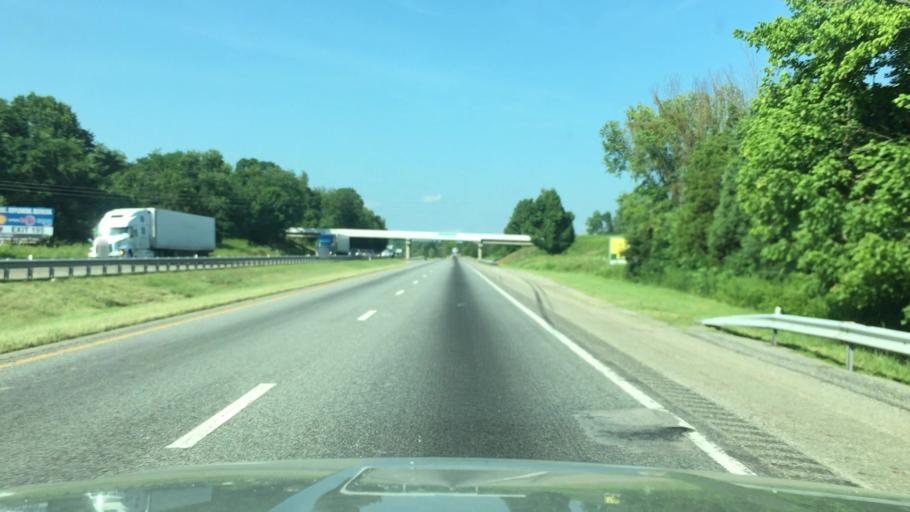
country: US
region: Virginia
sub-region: Botetourt County
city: Buchanan
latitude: 37.5929
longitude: -79.6303
